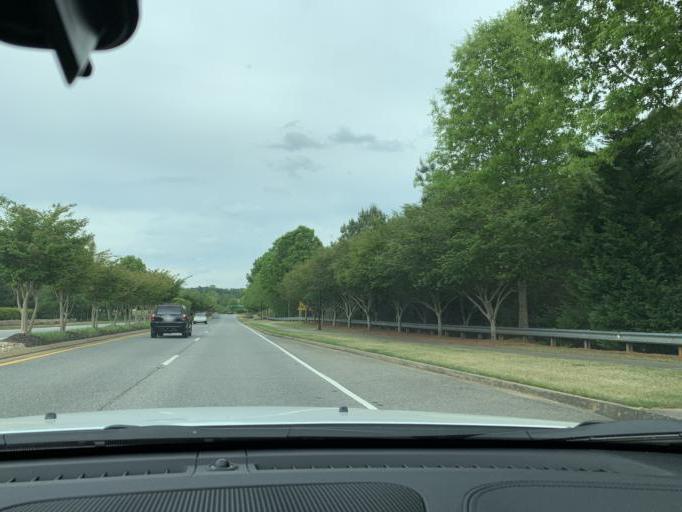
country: US
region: Georgia
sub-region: Forsyth County
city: Cumming
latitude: 34.1278
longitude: -84.1352
